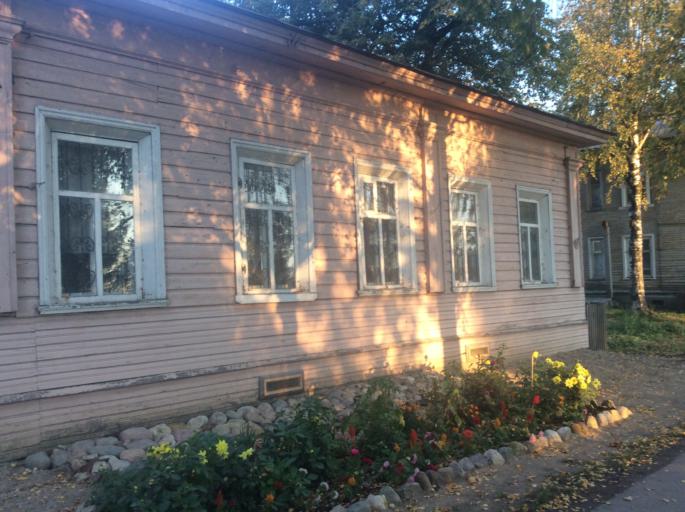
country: RU
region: Vologda
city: Kirillov
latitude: 59.8541
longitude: 38.3761
